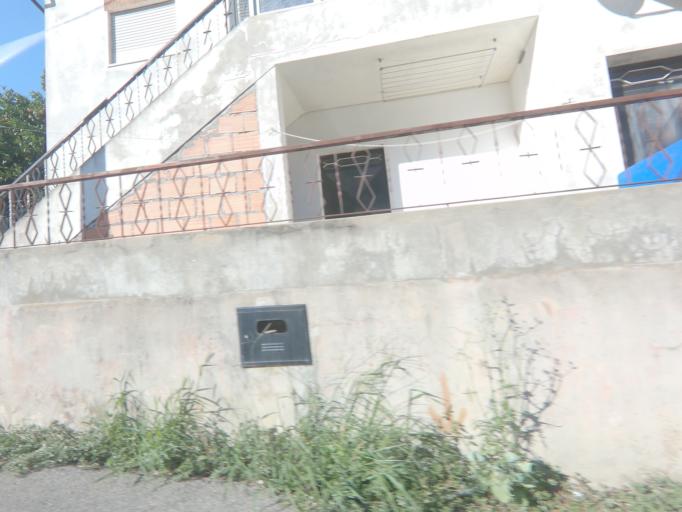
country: PT
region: Vila Real
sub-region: Sabrosa
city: Vilela
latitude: 41.1851
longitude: -7.5876
